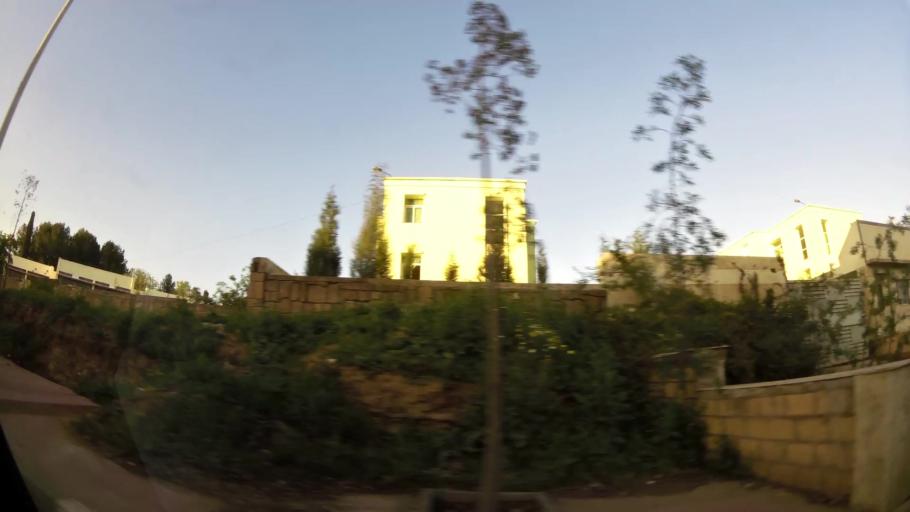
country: MA
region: Chaouia-Ouardigha
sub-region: Settat Province
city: Settat
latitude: 32.9900
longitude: -7.6111
